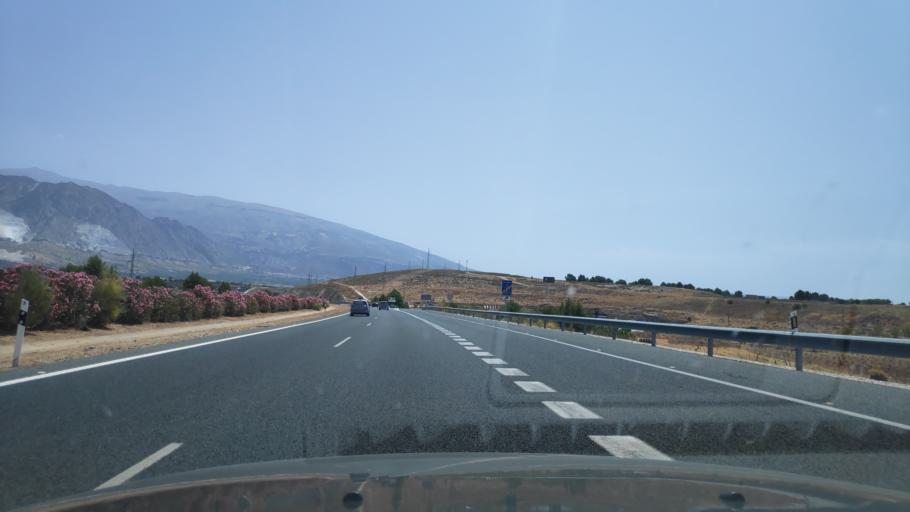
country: ES
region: Andalusia
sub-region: Provincia de Granada
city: Padul
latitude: 36.9888
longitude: -3.6096
